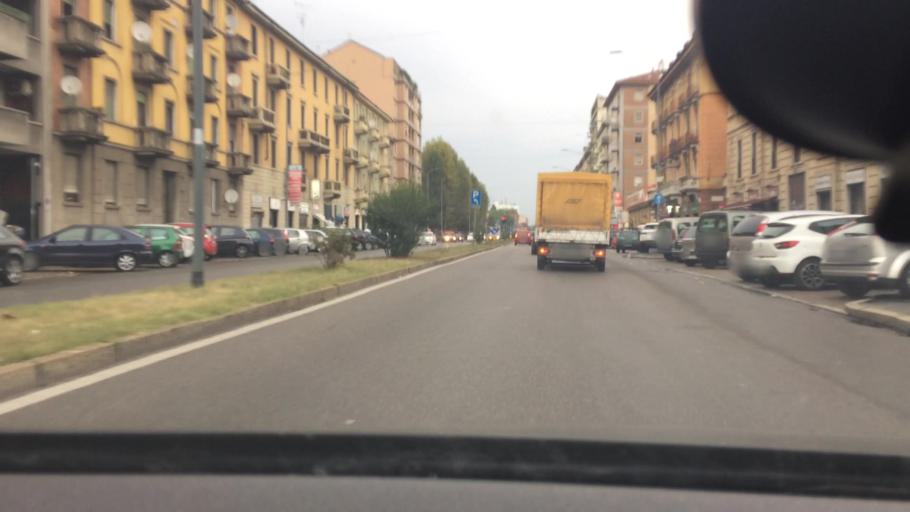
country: IT
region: Lombardy
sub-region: Citta metropolitana di Milano
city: Sesto San Giovanni
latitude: 45.5039
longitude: 9.2221
